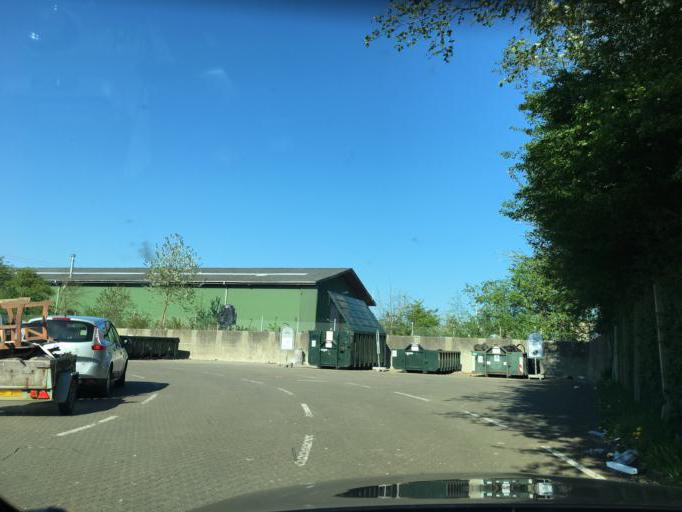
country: DK
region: South Denmark
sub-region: Kolding Kommune
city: Kolding
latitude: 55.5106
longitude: 9.4474
